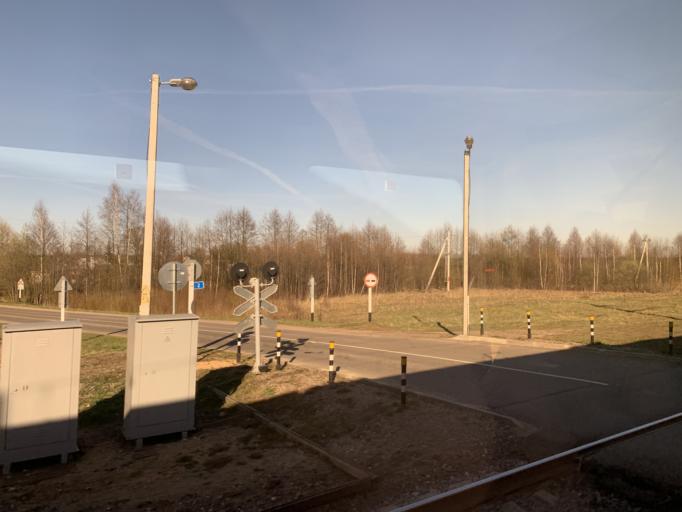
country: BY
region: Minsk
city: Turets-Bayary
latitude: 54.4186
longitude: 26.5457
